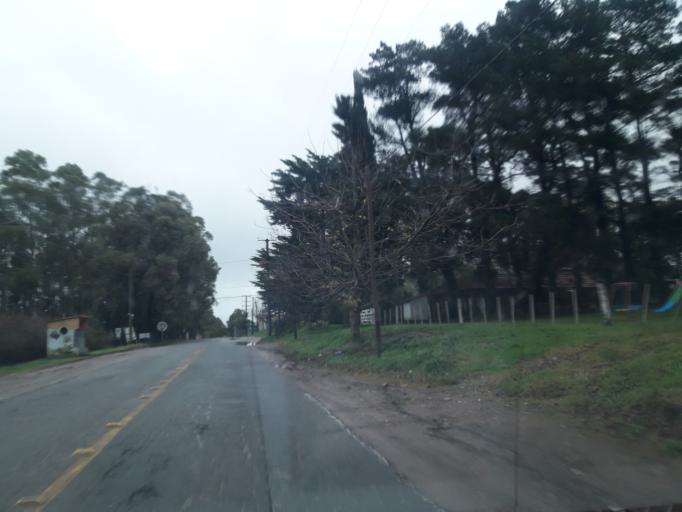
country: AR
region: Buenos Aires
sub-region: Partido de Tandil
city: Tandil
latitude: -37.3301
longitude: -59.1775
